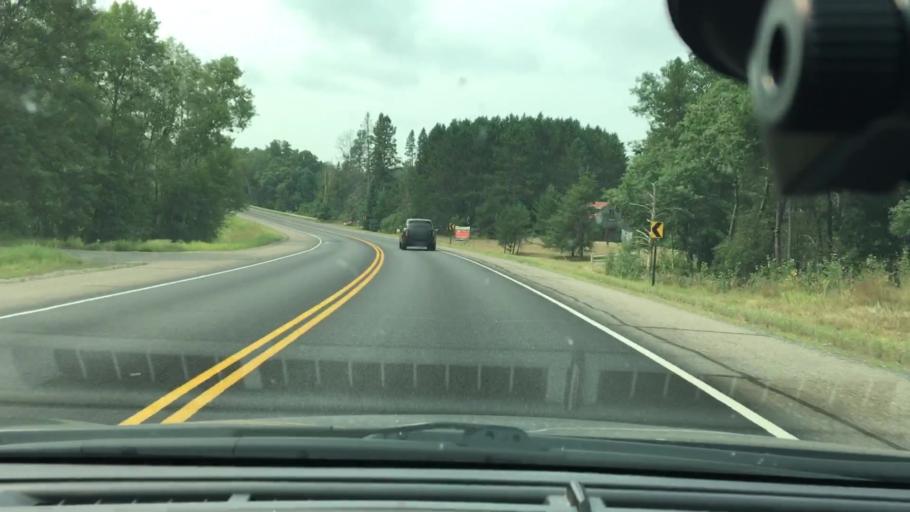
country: US
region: Minnesota
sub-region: Crow Wing County
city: Cross Lake
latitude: 46.6277
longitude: -94.1308
